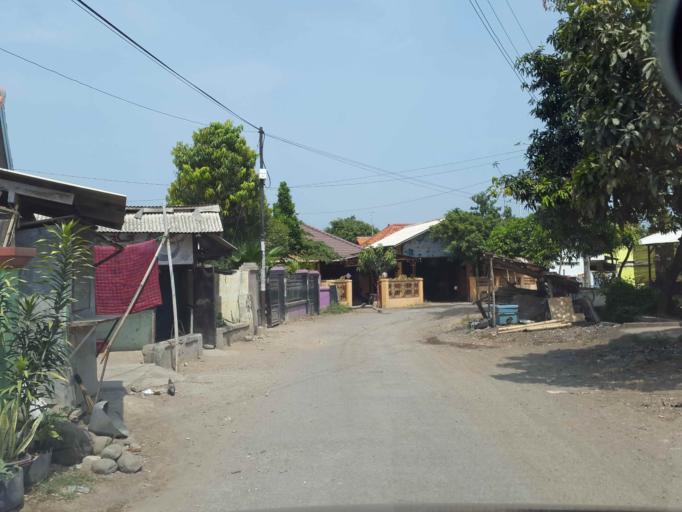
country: ID
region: Central Java
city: Dukuhturi
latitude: -6.8352
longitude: 109.0610
